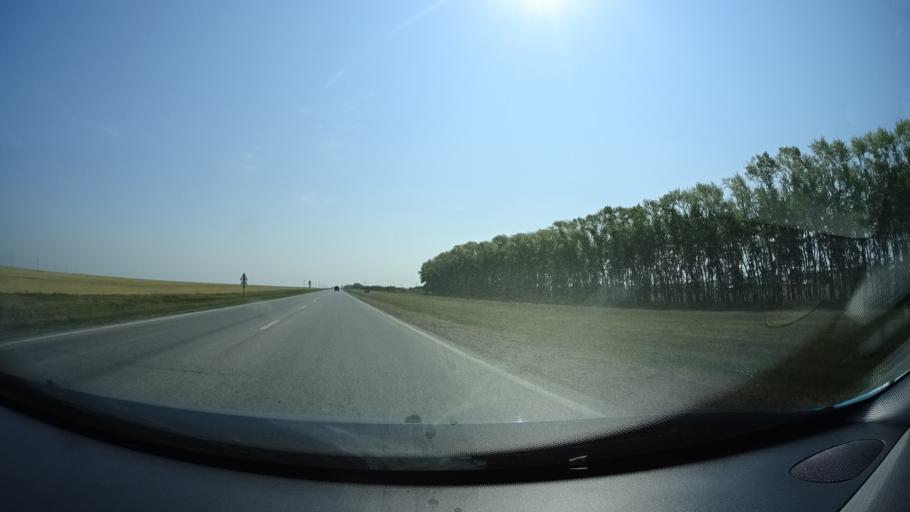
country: RU
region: Bashkortostan
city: Kabakovo
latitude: 54.4313
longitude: 56.0193
